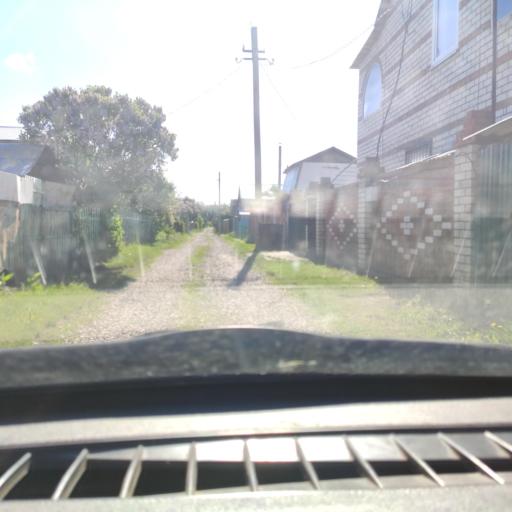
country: RU
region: Samara
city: Tol'yatti
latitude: 53.6269
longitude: 49.4084
